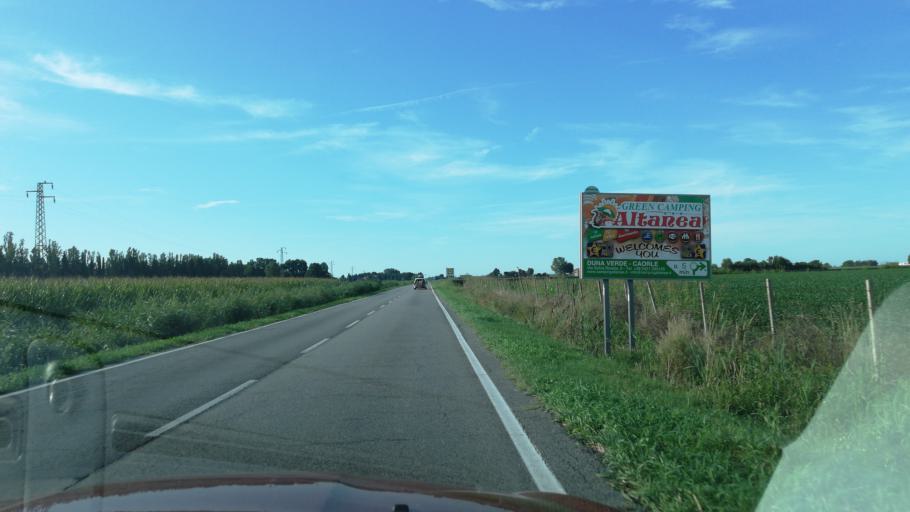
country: IT
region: Veneto
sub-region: Provincia di Venezia
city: San Giorgio di Livenza
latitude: 45.6144
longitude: 12.8022
